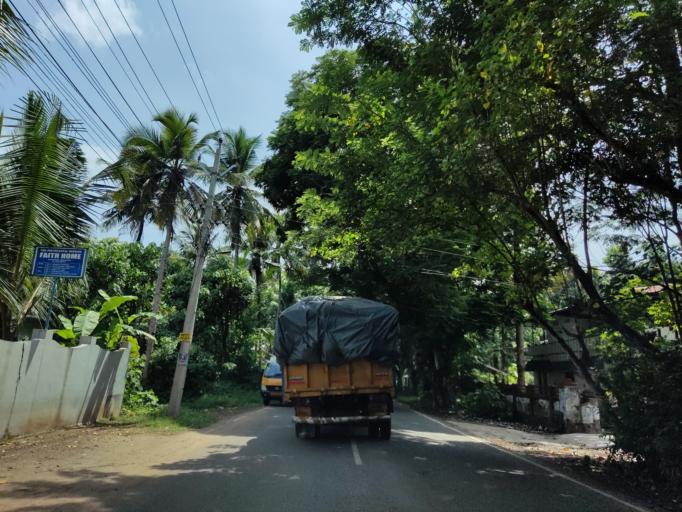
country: IN
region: Kerala
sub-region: Alappuzha
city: Chengannur
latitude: 9.3083
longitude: 76.5762
